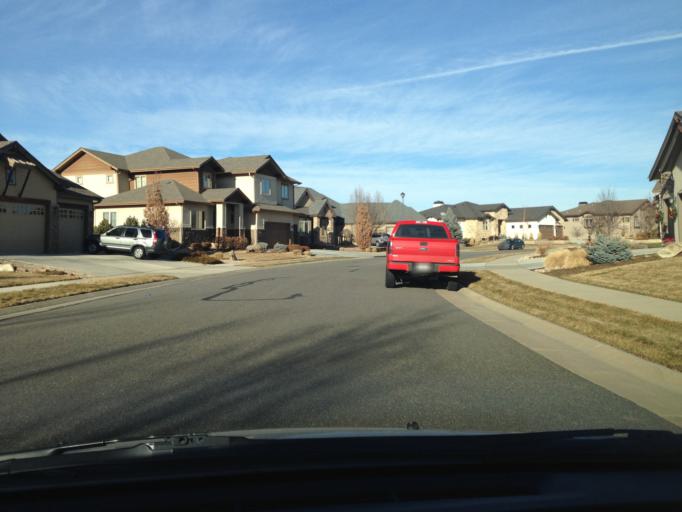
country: US
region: Colorado
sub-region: Boulder County
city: Erie
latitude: 40.0424
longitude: -105.0829
